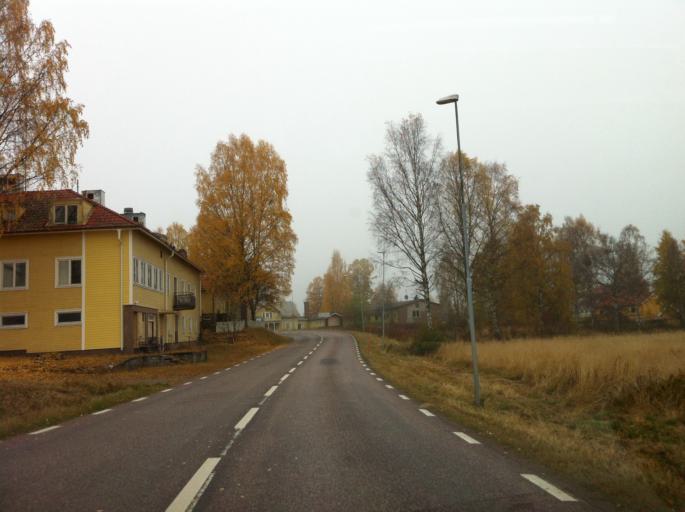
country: NO
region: Hedmark
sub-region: Trysil
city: Innbygda
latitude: 61.6912
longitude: 13.1503
